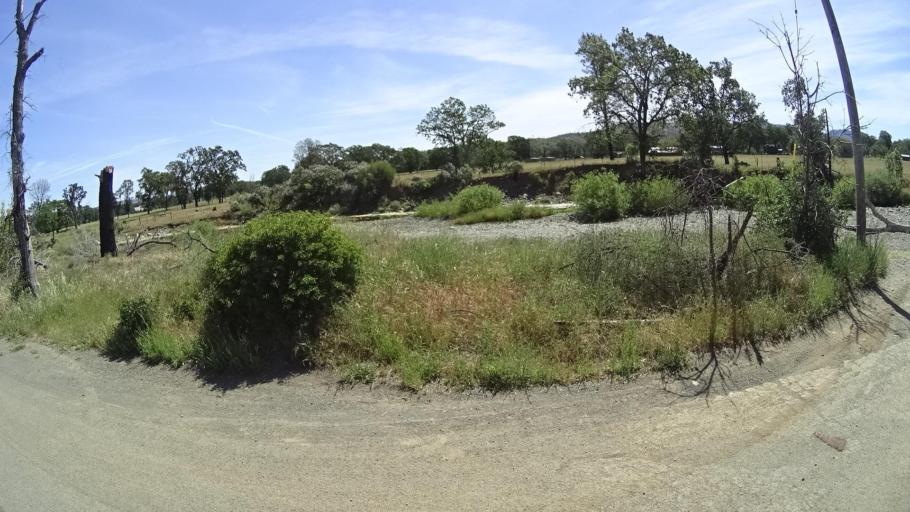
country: US
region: California
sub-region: Lake County
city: Middletown
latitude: 38.7441
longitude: -122.6329
